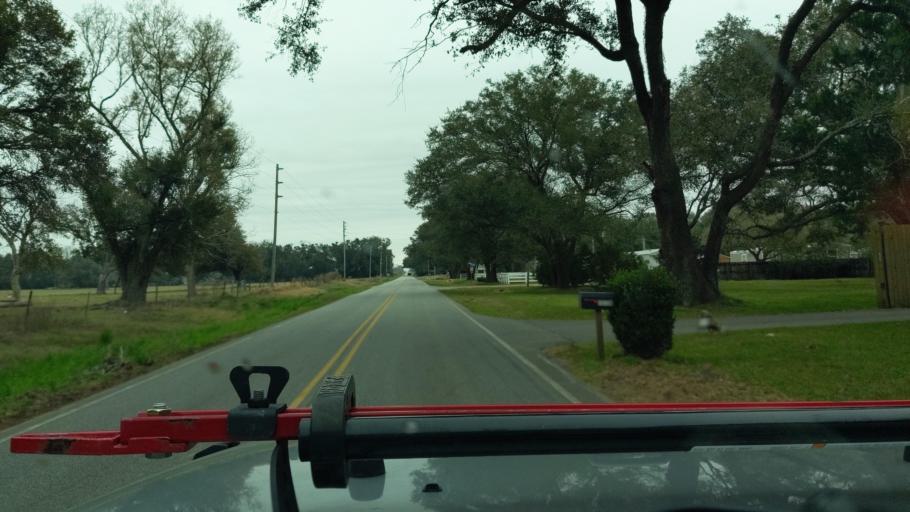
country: US
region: Alabama
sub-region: Baldwin County
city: Foley
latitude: 30.4579
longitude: -87.7656
